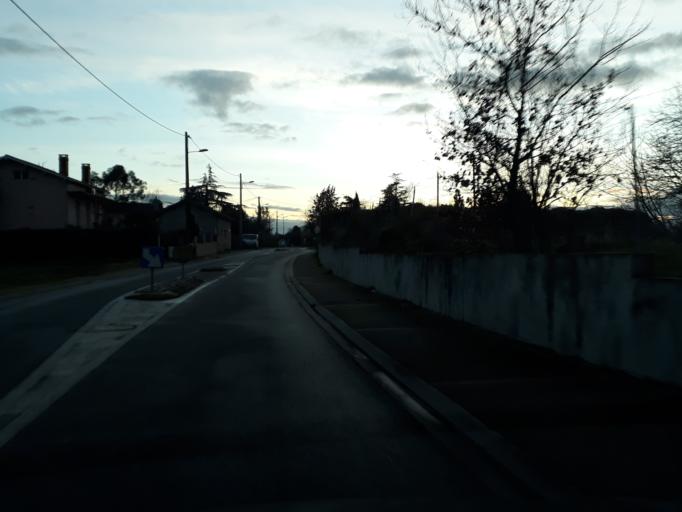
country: FR
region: Midi-Pyrenees
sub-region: Departement de la Haute-Garonne
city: Marquefave
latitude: 43.3140
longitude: 1.2385
